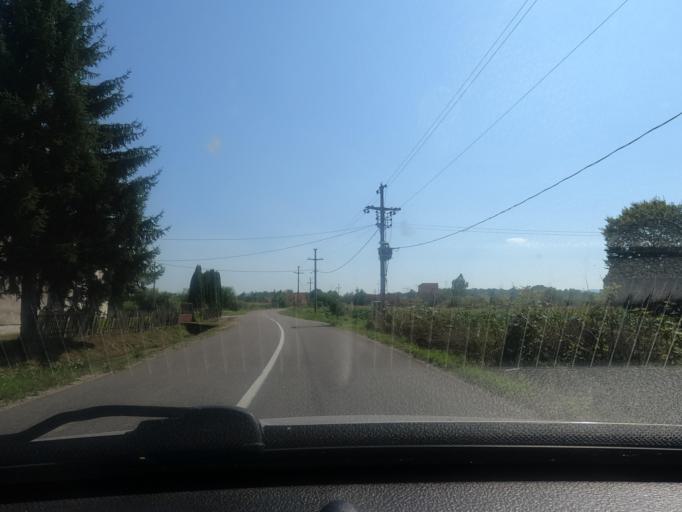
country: RS
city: Kozjak
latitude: 44.5489
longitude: 19.3091
